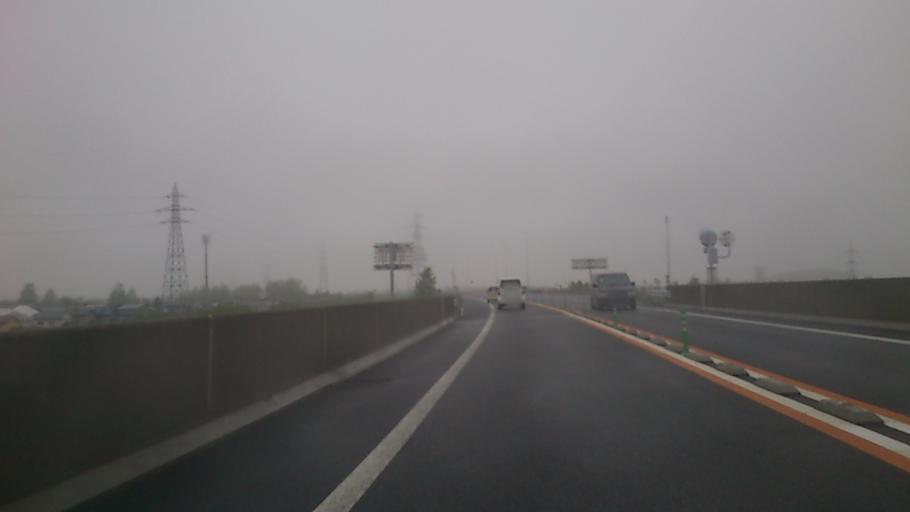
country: JP
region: Hokkaido
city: Kushiro
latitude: 43.0180
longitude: 144.4216
